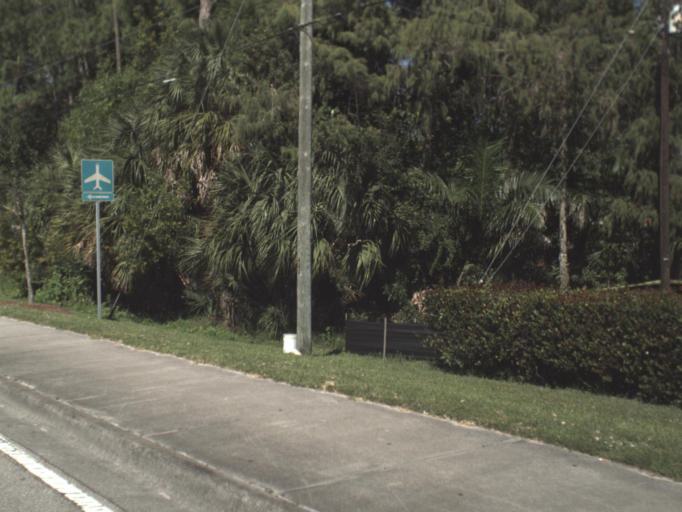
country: US
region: Florida
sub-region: Collier County
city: Pine Ridge
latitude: 26.2118
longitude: -81.7660
